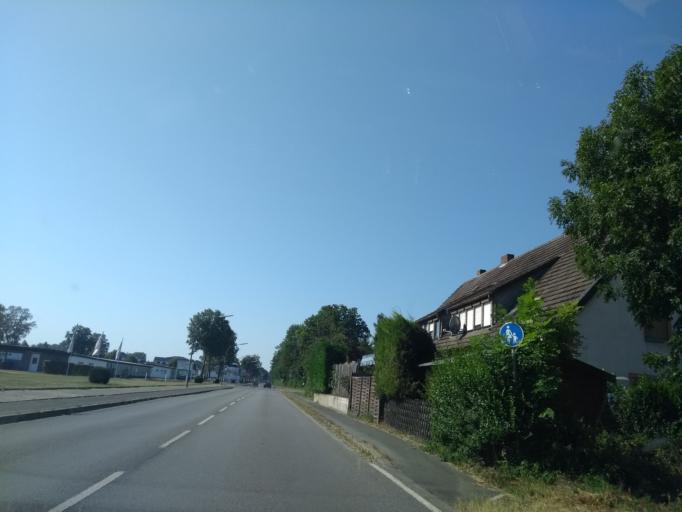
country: DE
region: North Rhine-Westphalia
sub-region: Regierungsbezirk Arnsberg
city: Lippstadt
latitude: 51.7152
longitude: 8.3686
